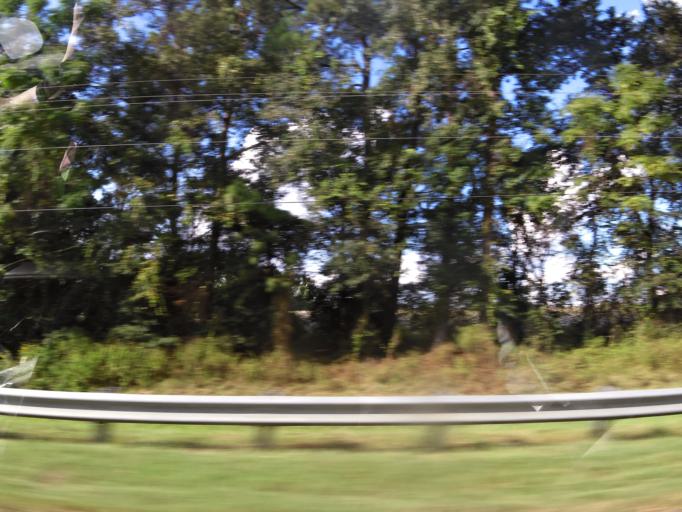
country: US
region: Georgia
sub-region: Brooks County
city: Quitman
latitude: 30.7853
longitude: -83.6140
